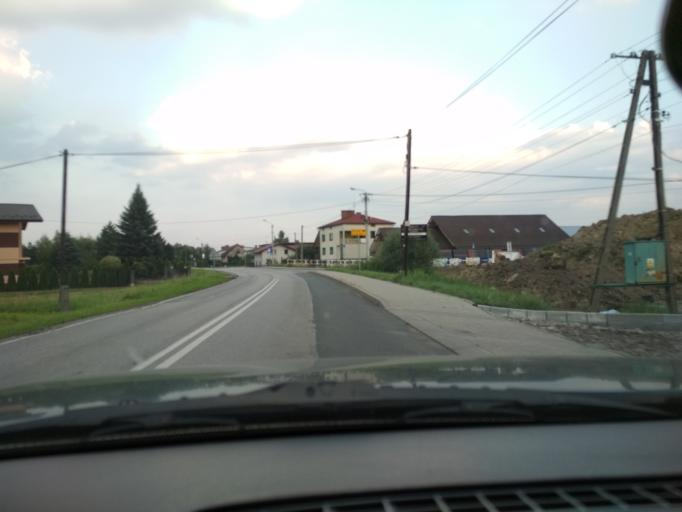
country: PL
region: Silesian Voivodeship
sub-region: Powiat cieszynski
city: Zablocie
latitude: 49.9026
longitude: 18.7811
